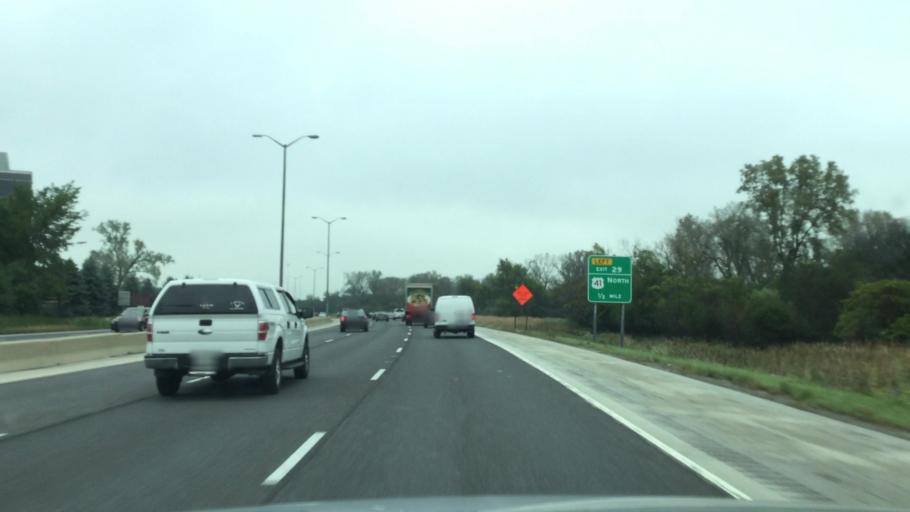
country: US
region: Illinois
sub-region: Cook County
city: Glencoe
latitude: 42.1315
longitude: -87.7852
